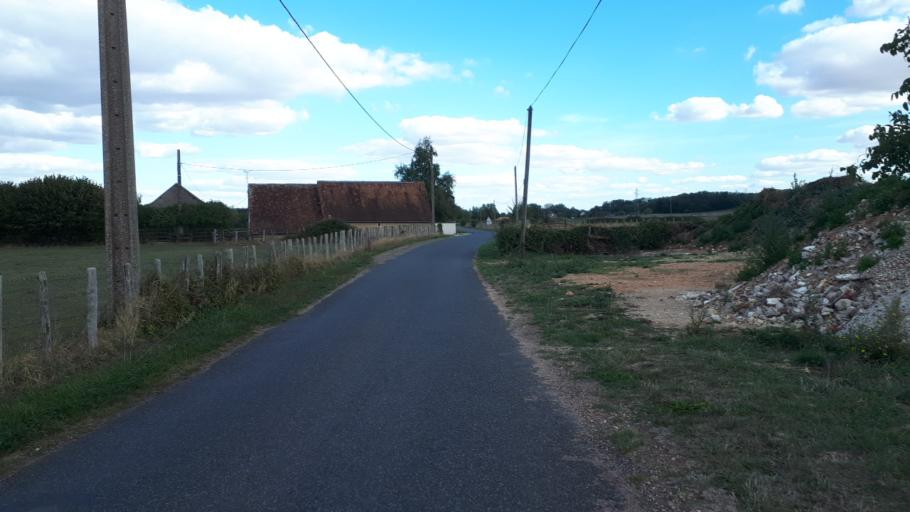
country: FR
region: Centre
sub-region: Departement du Loir-et-Cher
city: Villiers-sur-Loir
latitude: 47.8089
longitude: 0.9641
